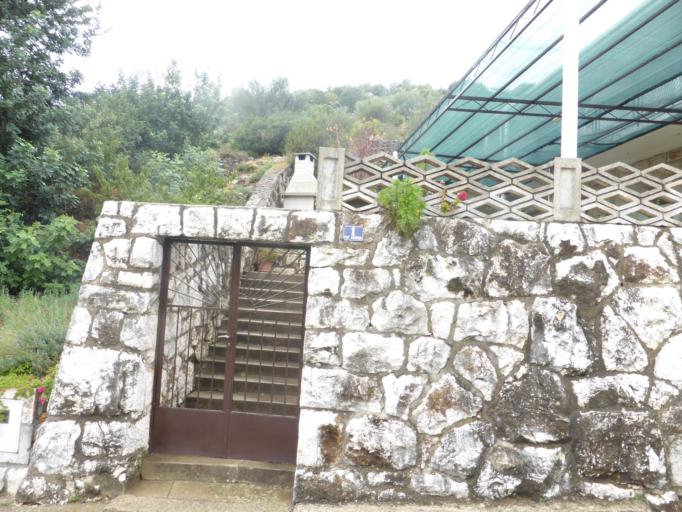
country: HR
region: Dubrovacko-Neretvanska
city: Podgora
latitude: 42.7862
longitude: 17.8788
